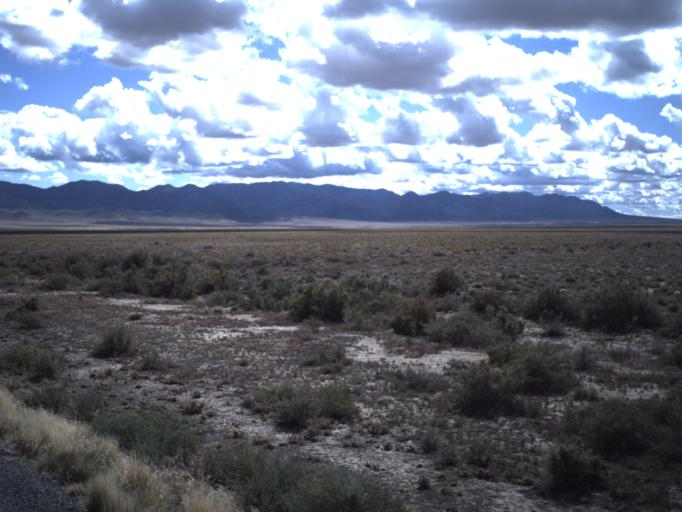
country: US
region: Utah
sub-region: Beaver County
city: Milford
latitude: 38.5457
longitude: -113.7180
